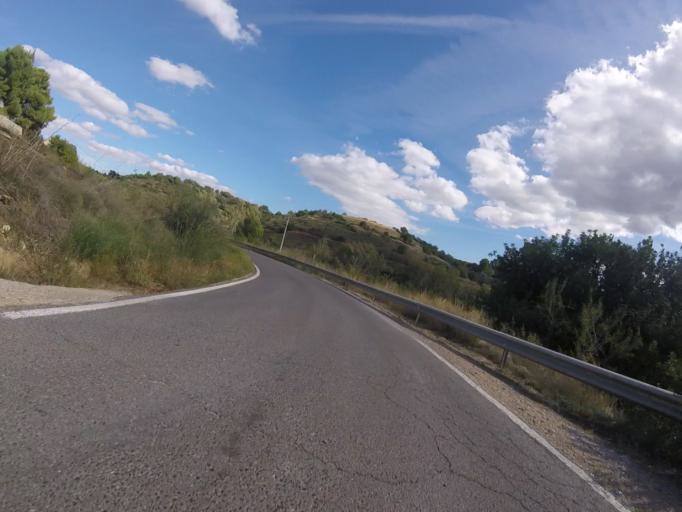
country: ES
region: Valencia
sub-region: Provincia de Castello
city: Cuevas de Vinroma
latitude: 40.3684
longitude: 0.1197
